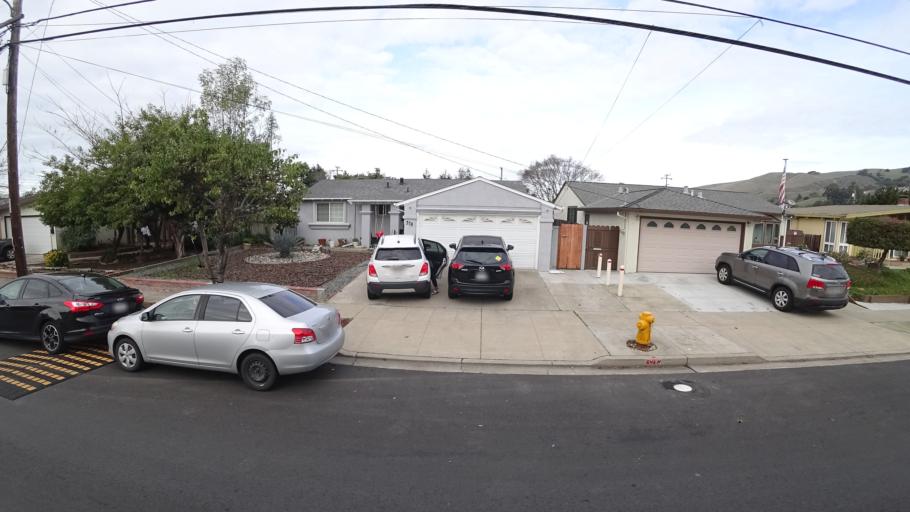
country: US
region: California
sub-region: Alameda County
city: Union City
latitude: 37.6212
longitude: -122.0399
